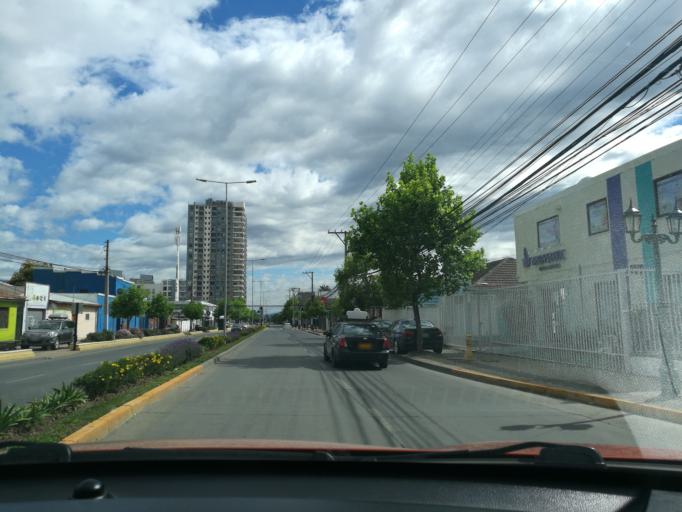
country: CL
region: O'Higgins
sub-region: Provincia de Cachapoal
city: Rancagua
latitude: -34.1733
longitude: -70.7358
